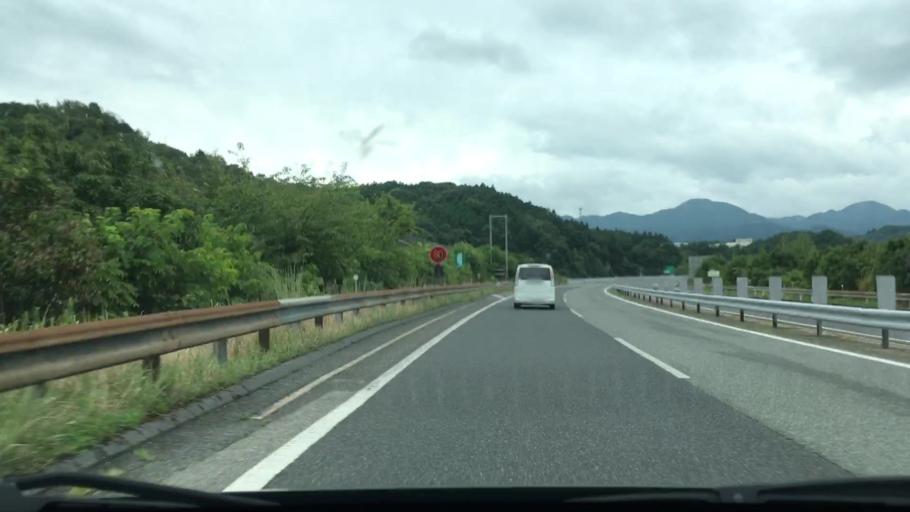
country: JP
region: Hiroshima
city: Hiroshima-shi
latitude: 34.6759
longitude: 132.5576
